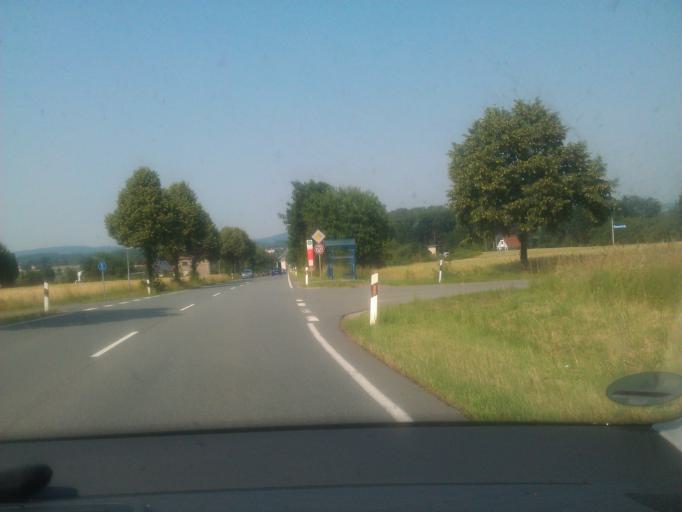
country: DE
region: North Rhine-Westphalia
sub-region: Regierungsbezirk Detmold
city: Leopoldshohe
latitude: 52.0198
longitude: 8.7110
